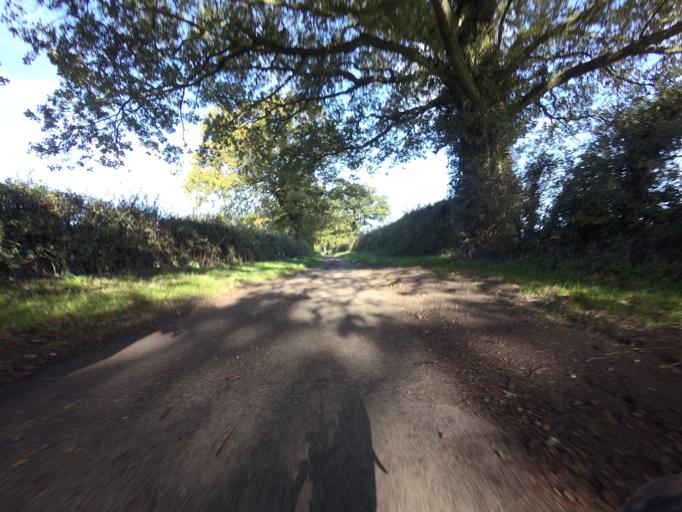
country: GB
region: England
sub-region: Norfolk
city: Fakenham
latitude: 52.8447
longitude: 0.6807
